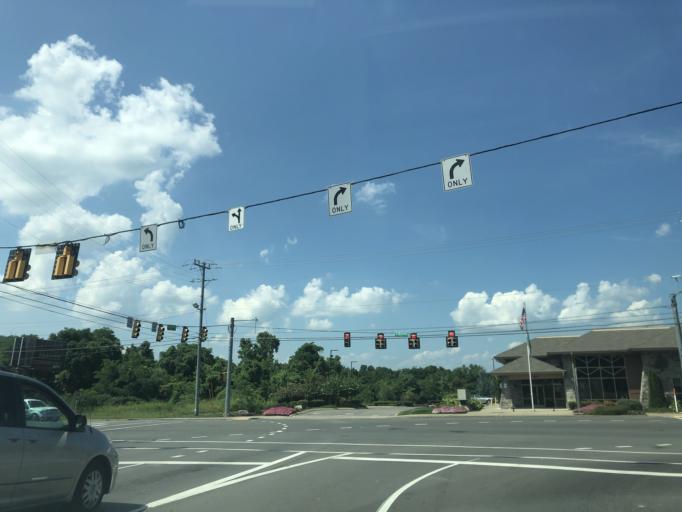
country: US
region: Tennessee
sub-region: Davidson County
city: Lakewood
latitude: 36.1674
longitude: -86.6632
